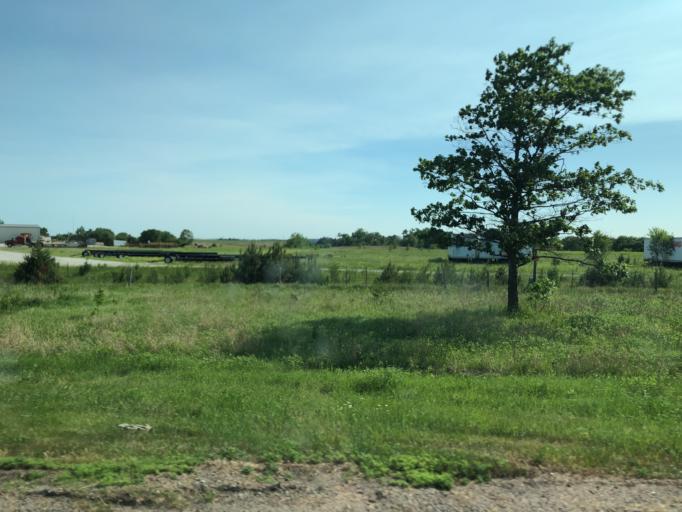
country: US
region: Nebraska
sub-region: Seward County
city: Milford
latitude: 40.8210
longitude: -97.1032
